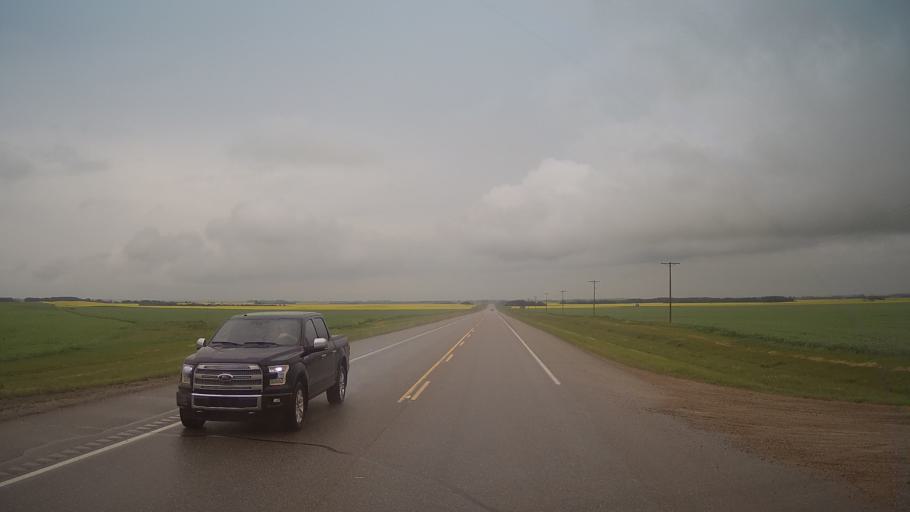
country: CA
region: Saskatchewan
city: Wilkie
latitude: 52.4197
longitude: -108.8933
